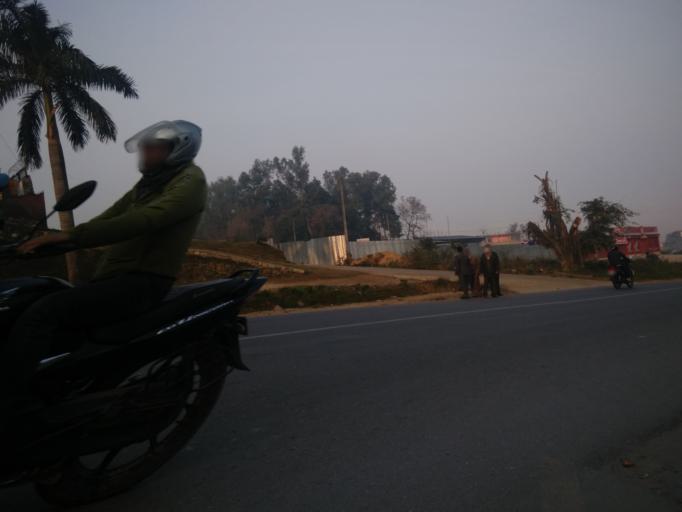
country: NP
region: Central Region
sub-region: Narayani Zone
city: Bharatpur
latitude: 27.6888
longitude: 84.4278
